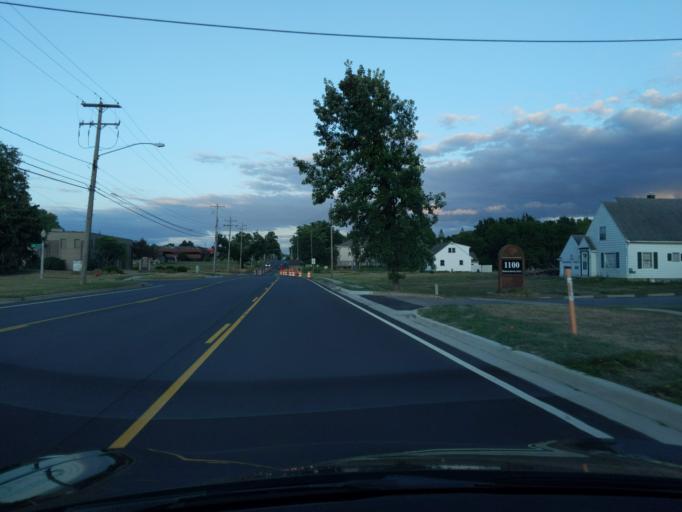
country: US
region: Michigan
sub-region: Ingham County
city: Holt
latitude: 42.6692
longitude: -84.5366
